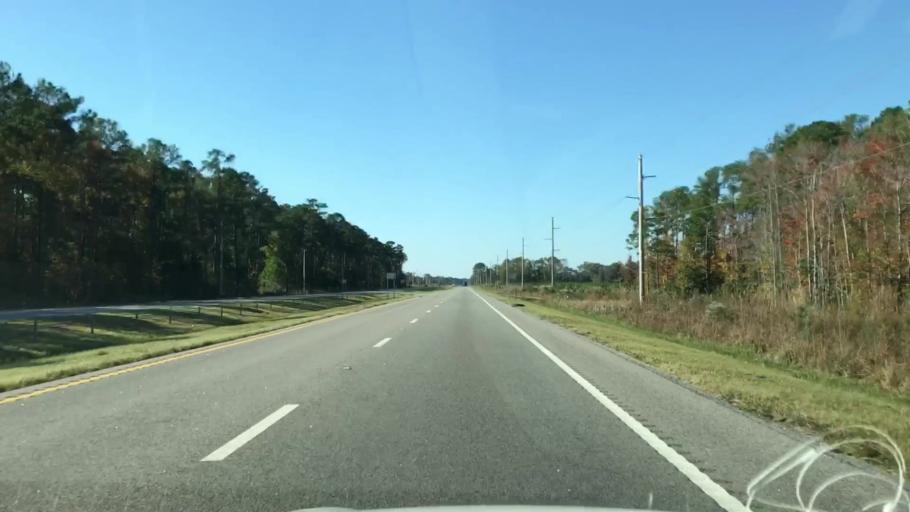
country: US
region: South Carolina
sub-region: Colleton County
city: Walterboro
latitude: 32.7548
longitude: -80.5341
